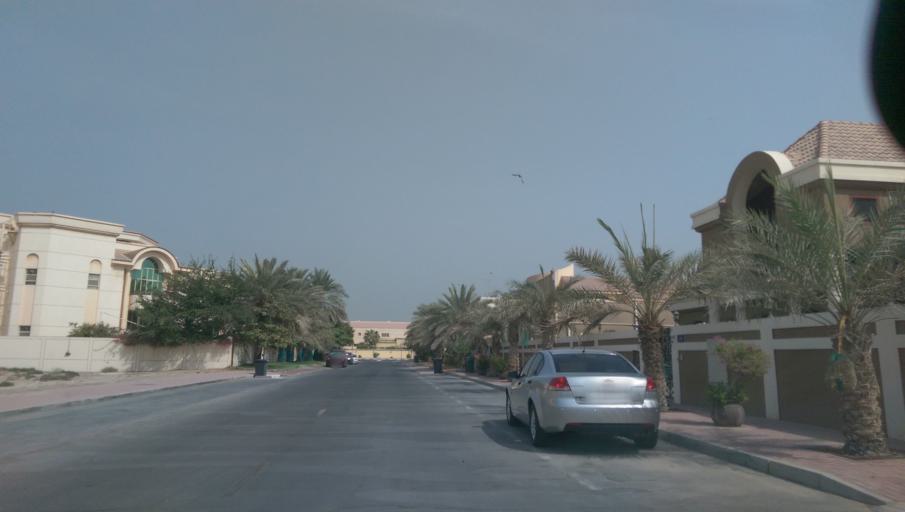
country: AE
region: Dubai
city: Dubai
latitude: 25.1569
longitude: 55.2249
